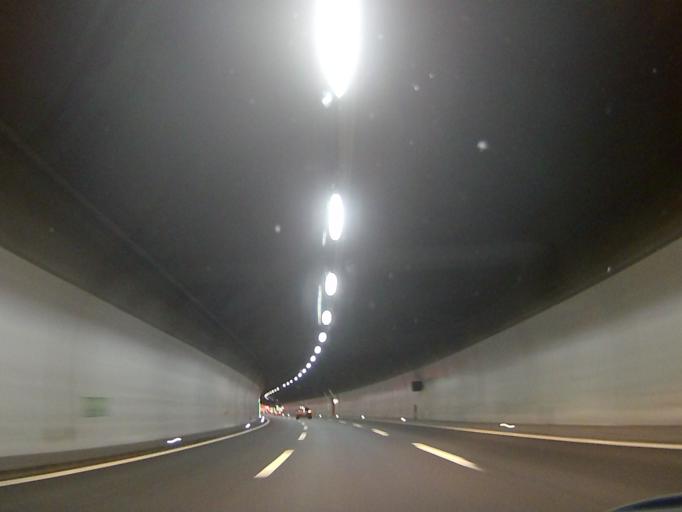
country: CH
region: Ticino
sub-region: Leventina District
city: Faido
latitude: 46.4897
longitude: 8.7553
